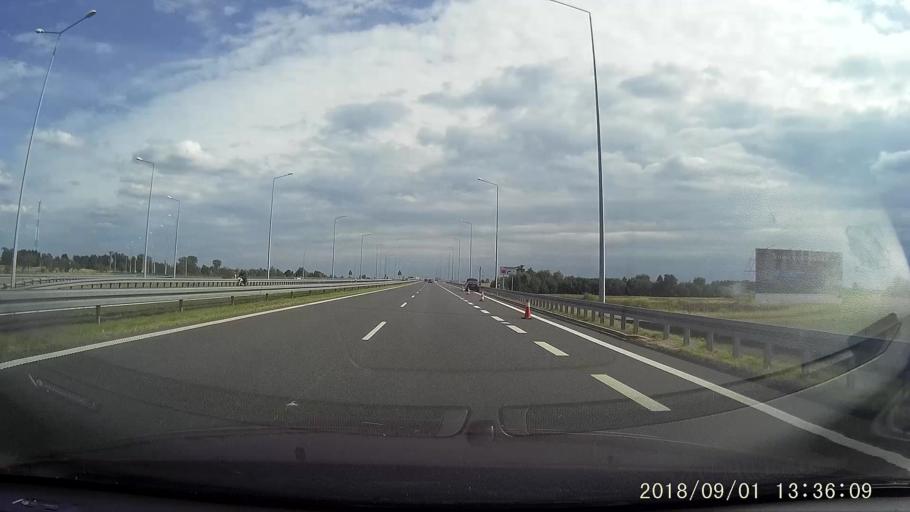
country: PL
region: West Pomeranian Voivodeship
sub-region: Powiat pyrzycki
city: Lipiany
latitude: 52.9533
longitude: 14.9442
